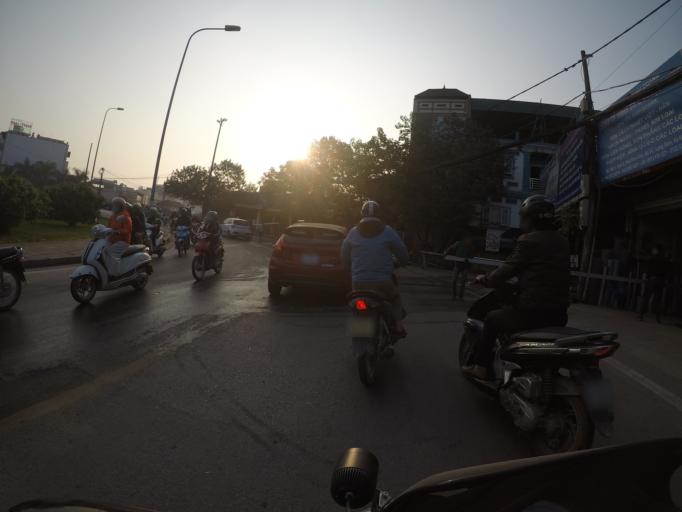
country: VN
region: Ha Noi
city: Hoan Kiem
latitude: 21.0393
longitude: 105.8656
